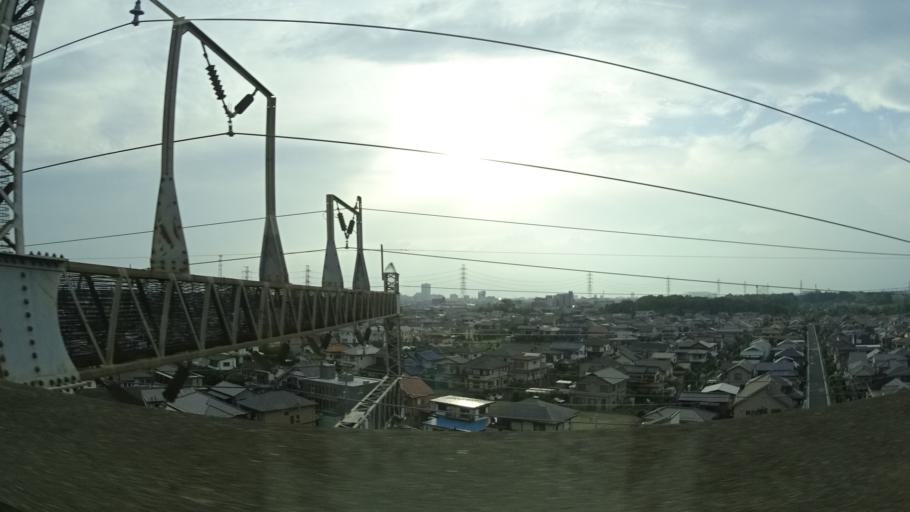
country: JP
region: Saitama
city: Ageoshimo
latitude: 35.9733
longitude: 139.6242
